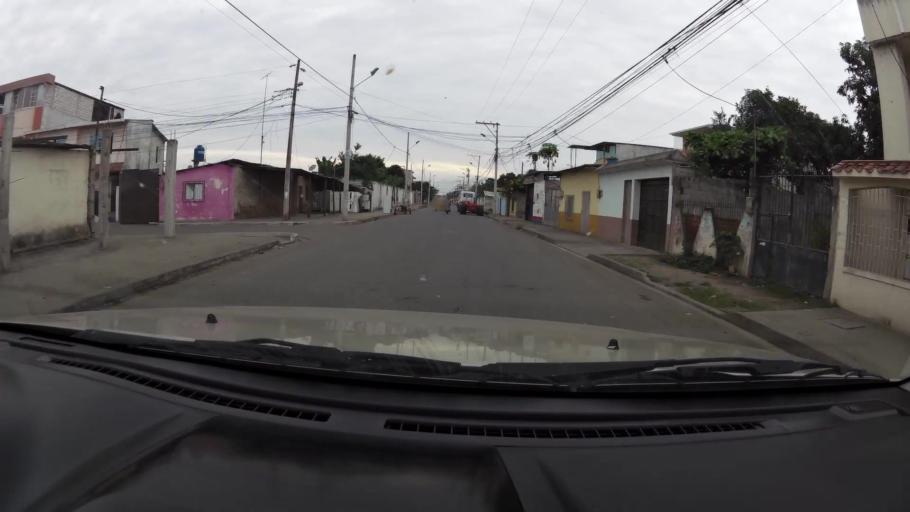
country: EC
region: El Oro
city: Machala
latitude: -3.2572
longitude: -79.9417
